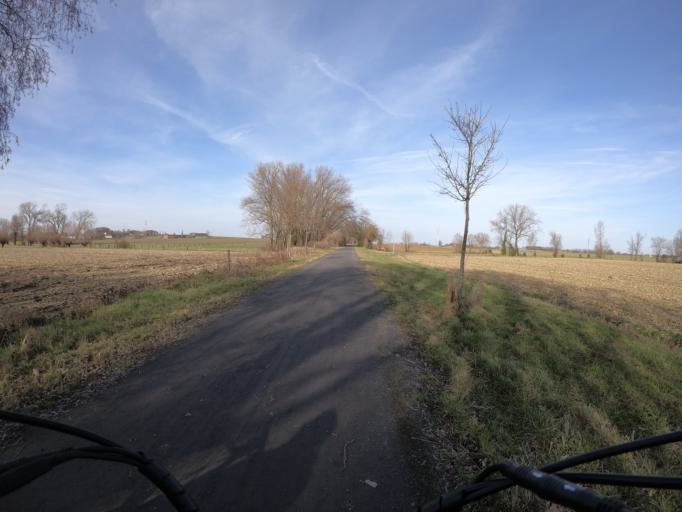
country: BE
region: Flanders
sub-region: Provincie West-Vlaanderen
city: Ledegem
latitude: 50.8276
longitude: 3.1243
